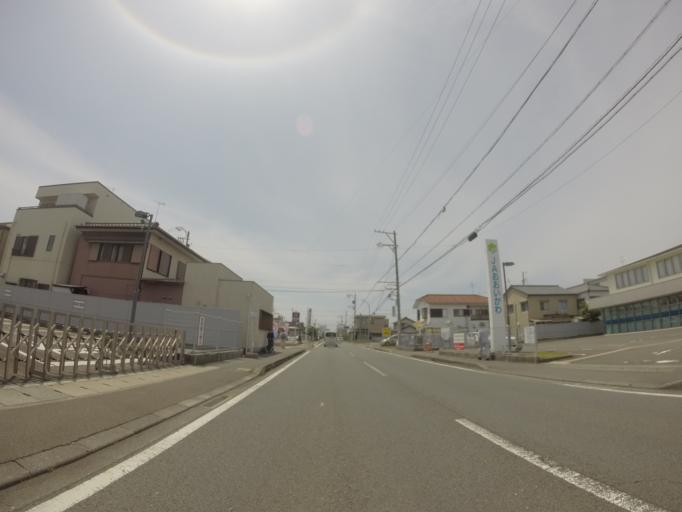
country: JP
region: Shizuoka
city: Yaizu
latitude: 34.8631
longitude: 138.3144
